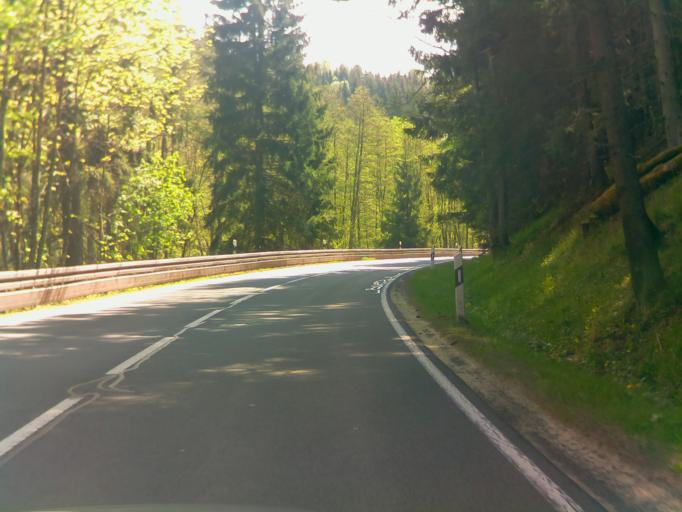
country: DE
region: Saxony-Anhalt
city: Hasselfelde
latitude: 51.6486
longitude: 10.8207
